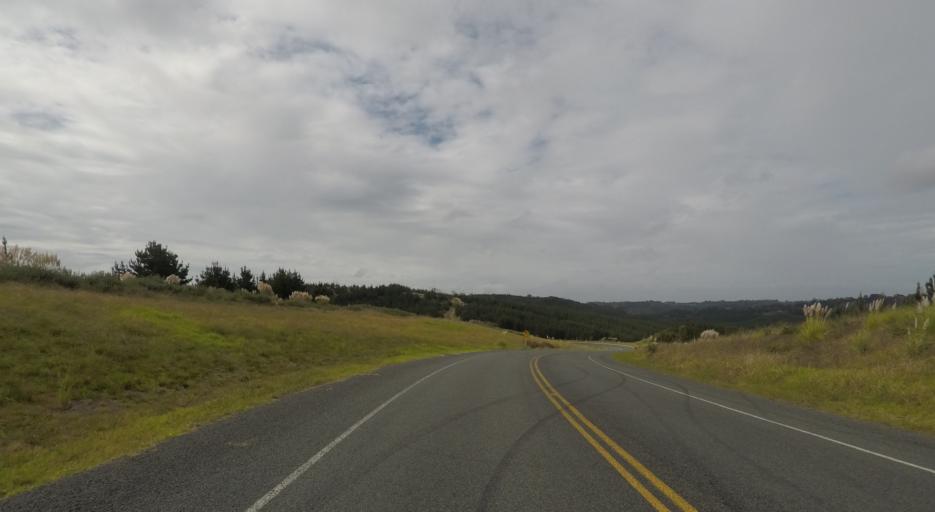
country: NZ
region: Auckland
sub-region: Auckland
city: Rothesay Bay
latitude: -36.6543
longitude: 174.6974
